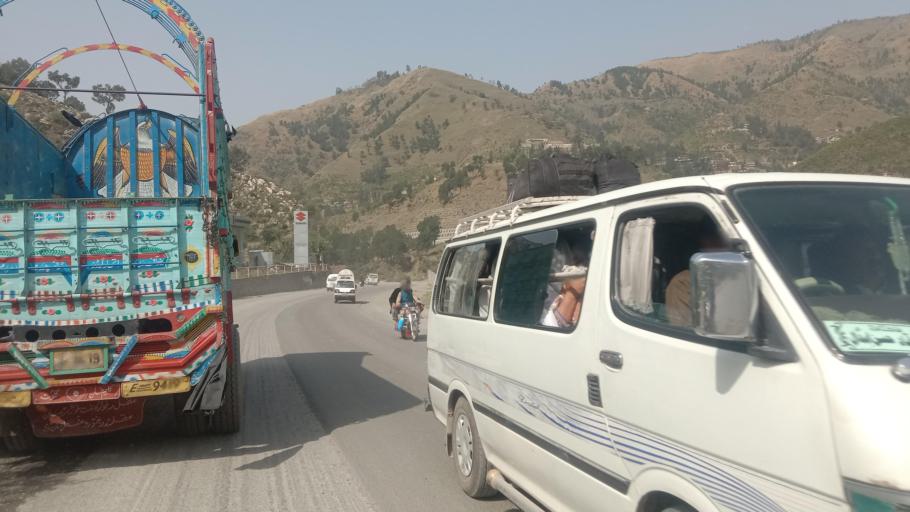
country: PK
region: Khyber Pakhtunkhwa
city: Abbottabad
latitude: 34.1235
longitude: 73.1901
